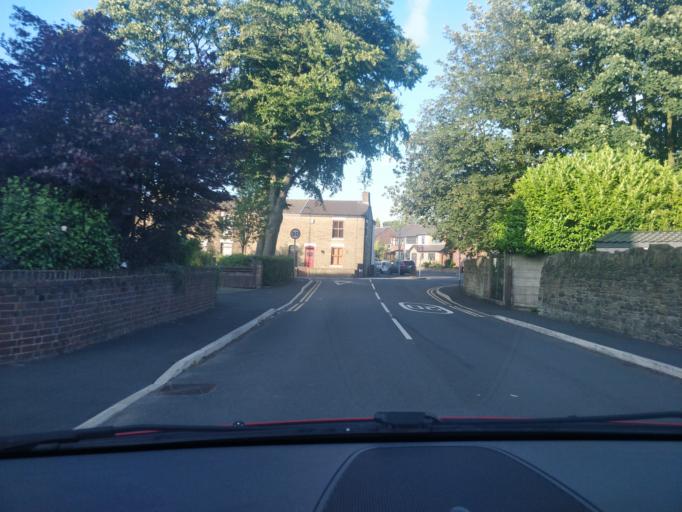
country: GB
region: England
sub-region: St. Helens
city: Billinge
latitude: 53.5221
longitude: -2.7164
